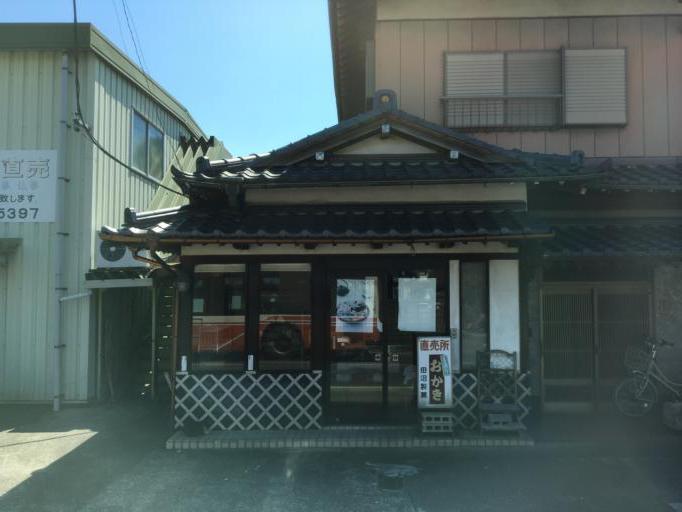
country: JP
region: Saitama
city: Kawagoe
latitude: 35.9509
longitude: 139.4877
